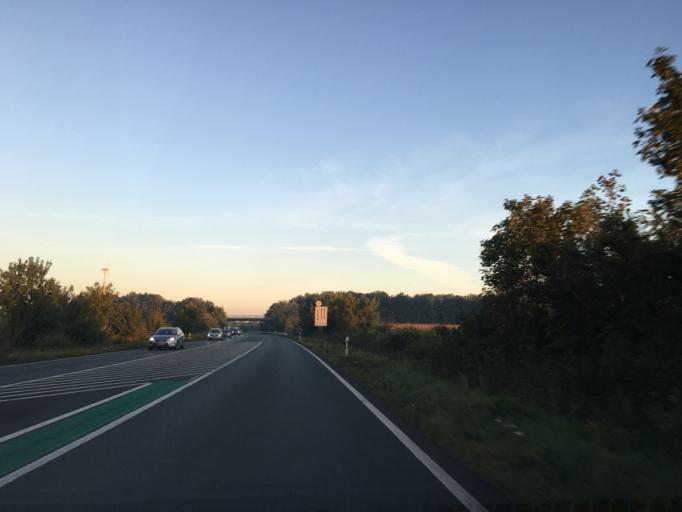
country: DE
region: North Rhine-Westphalia
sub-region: Regierungsbezirk Munster
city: Laer
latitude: 52.0944
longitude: 7.4105
